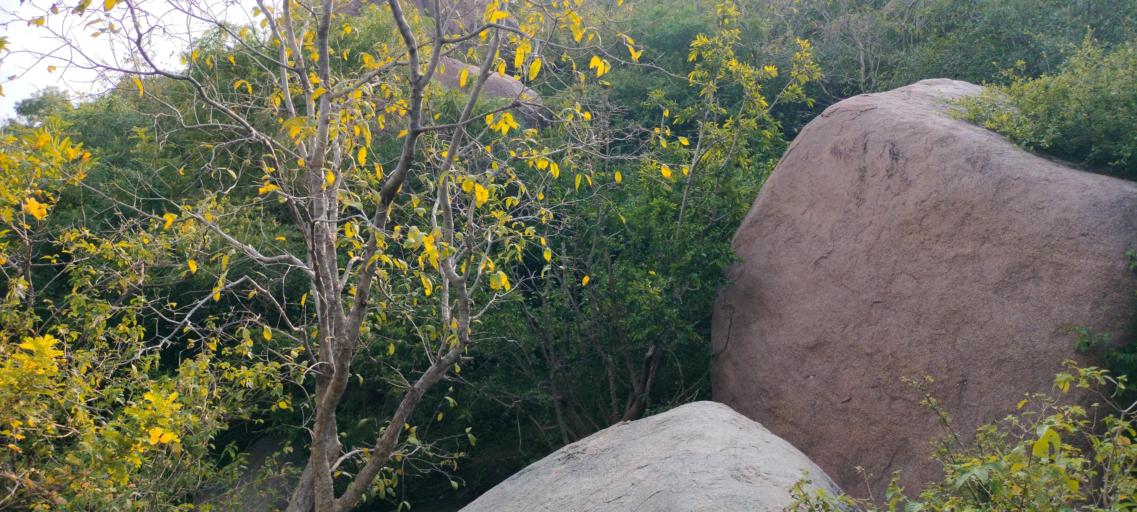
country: IN
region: Telangana
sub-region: Mahbubnagar
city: Farrukhnagar
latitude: 16.8931
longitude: 78.4916
